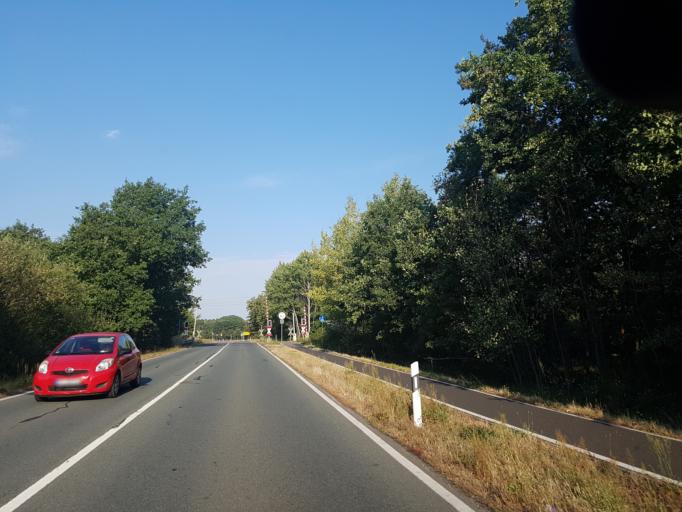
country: DE
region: Saxony
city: Nauwalde
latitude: 51.3927
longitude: 13.4175
